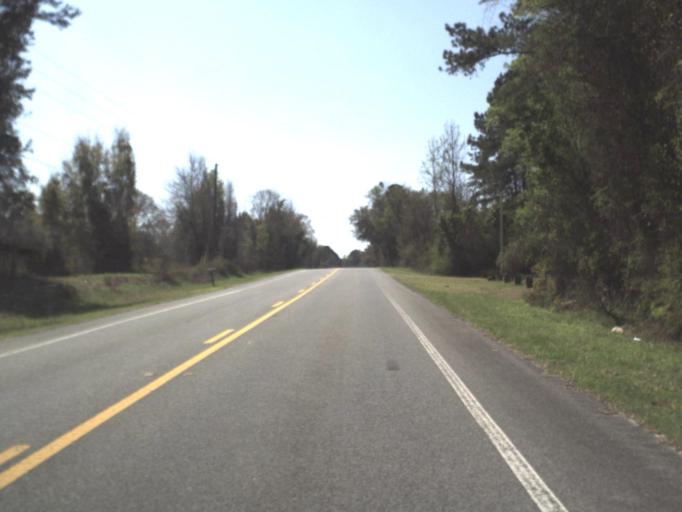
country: US
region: Florida
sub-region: Jefferson County
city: Monticello
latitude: 30.5103
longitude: -84.0243
